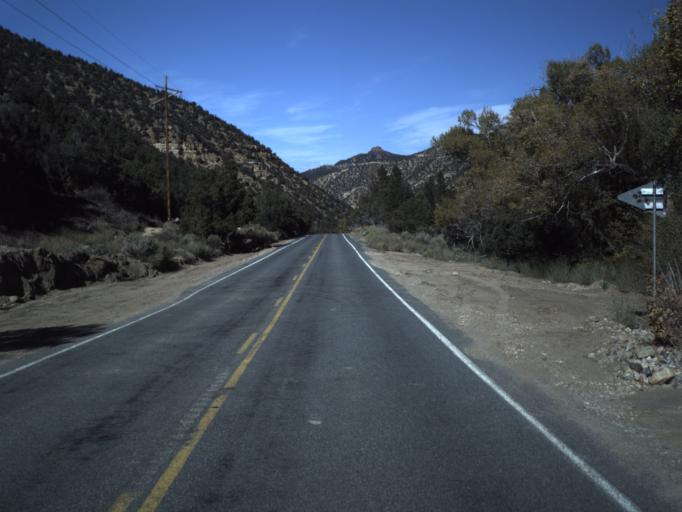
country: US
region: Utah
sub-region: Iron County
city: Parowan
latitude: 37.7845
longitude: -112.8281
